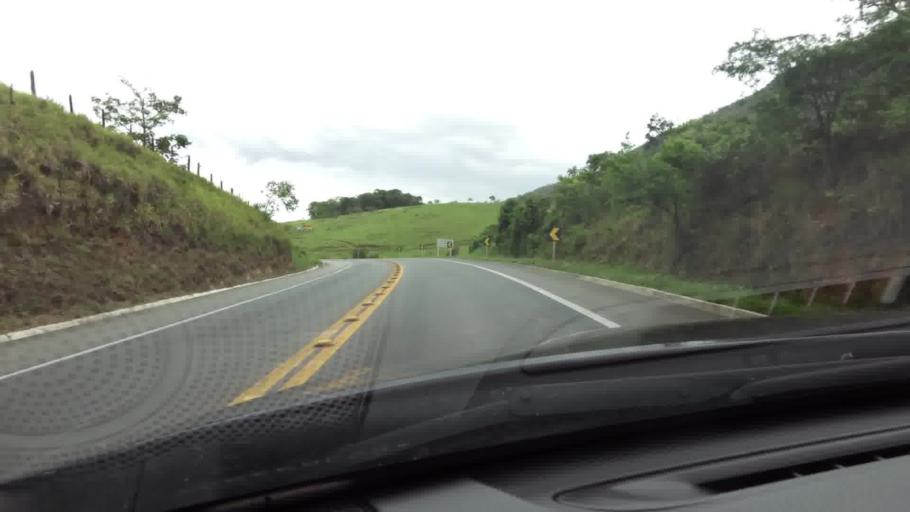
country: BR
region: Espirito Santo
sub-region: Guarapari
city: Guarapari
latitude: -20.6073
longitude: -40.5090
